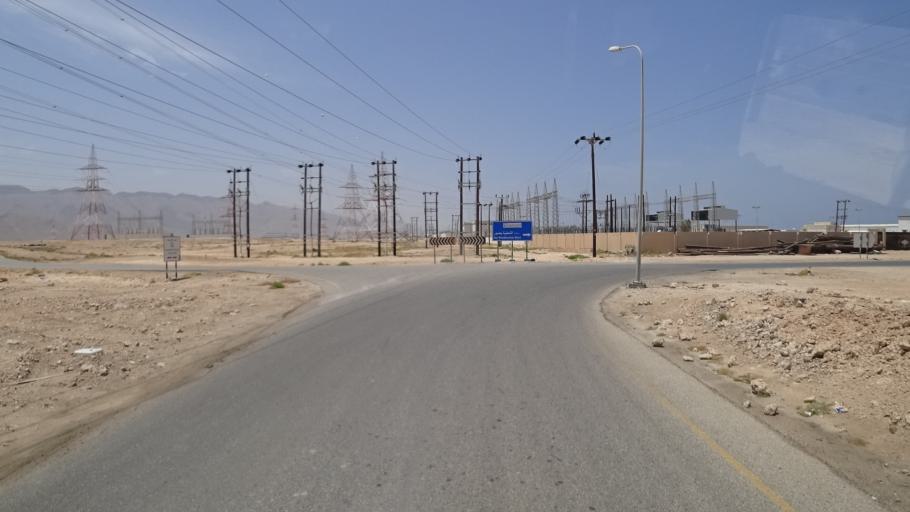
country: OM
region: Ash Sharqiyah
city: Sur
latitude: 22.6171
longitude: 59.4540
